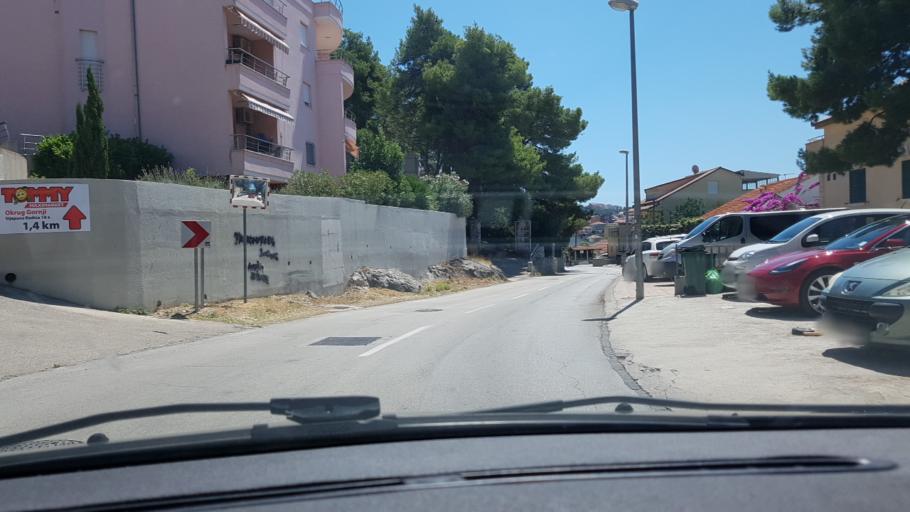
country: HR
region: Splitsko-Dalmatinska
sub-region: Grad Trogir
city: Trogir
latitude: 43.5106
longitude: 16.2544
